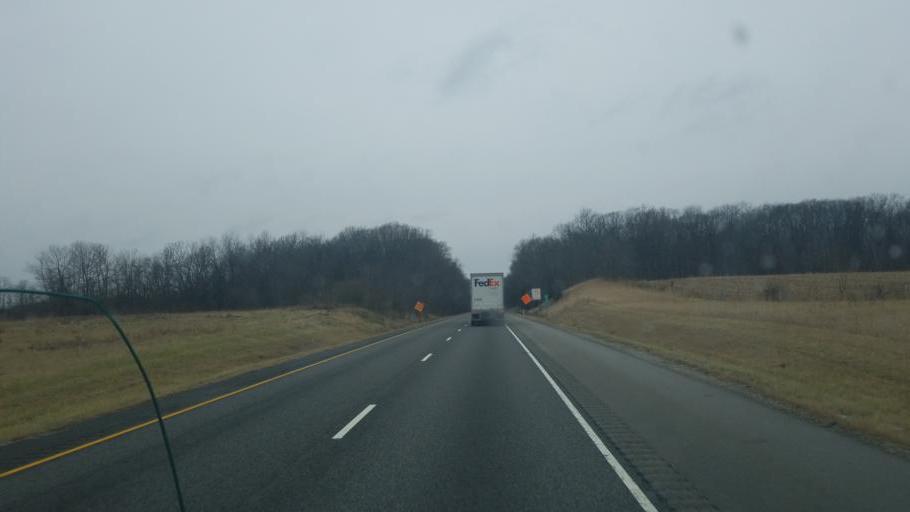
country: US
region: Indiana
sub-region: Henry County
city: New Castle
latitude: 39.8538
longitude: -85.4318
